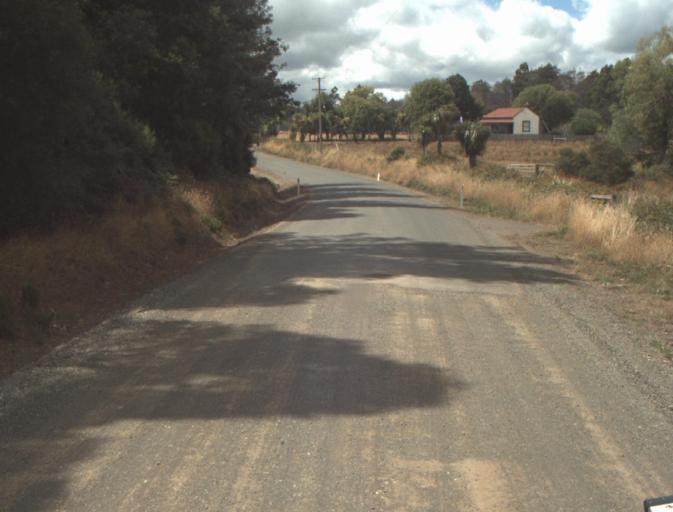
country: AU
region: Tasmania
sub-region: Launceston
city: Mayfield
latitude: -41.1946
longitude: 147.1990
